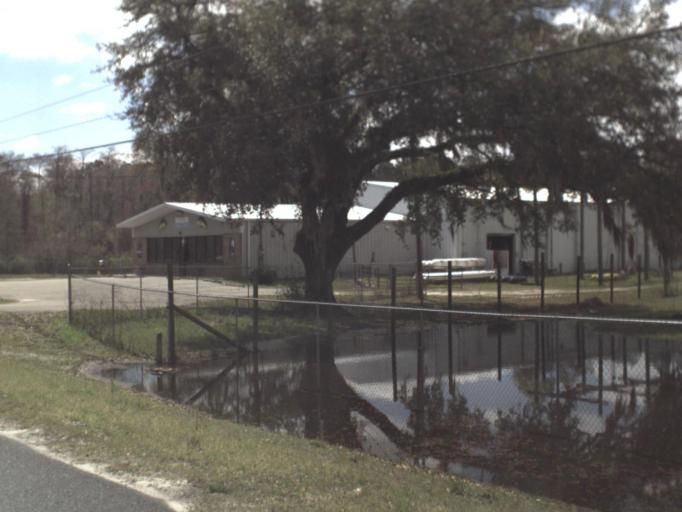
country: US
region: Florida
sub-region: Wakulla County
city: Crawfordville
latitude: 30.0901
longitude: -84.3859
